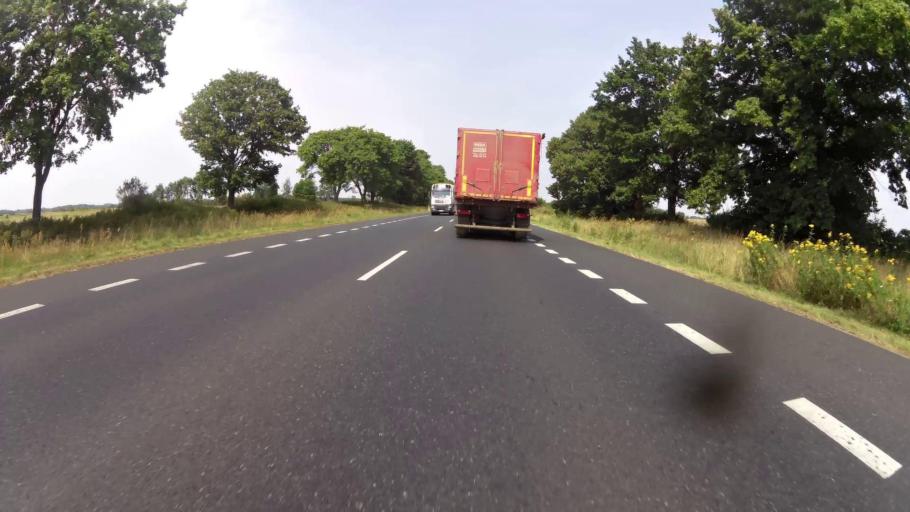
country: PL
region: West Pomeranian Voivodeship
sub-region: Powiat pyrzycki
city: Lipiany
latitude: 52.9659
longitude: 14.9685
